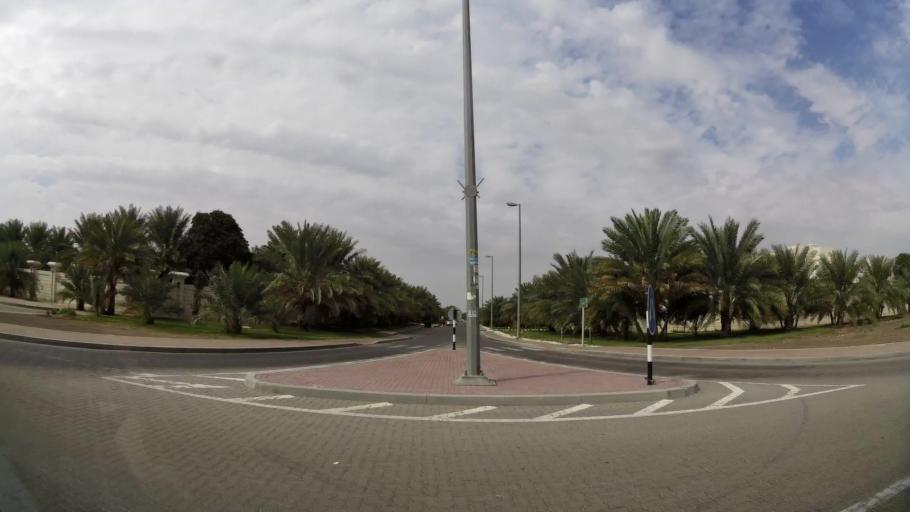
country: AE
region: Abu Dhabi
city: Al Ain
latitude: 24.1920
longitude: 55.8048
